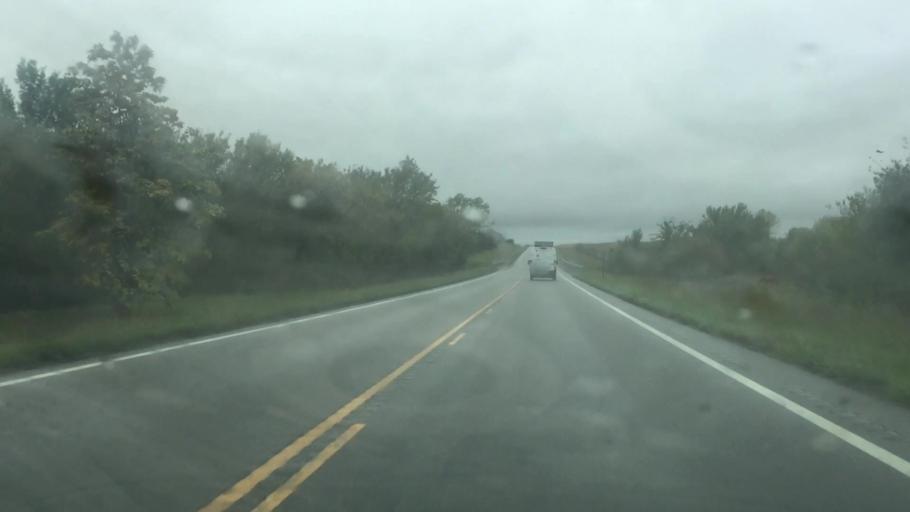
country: US
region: Kansas
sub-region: Anderson County
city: Garnett
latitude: 38.1518
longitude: -95.3168
